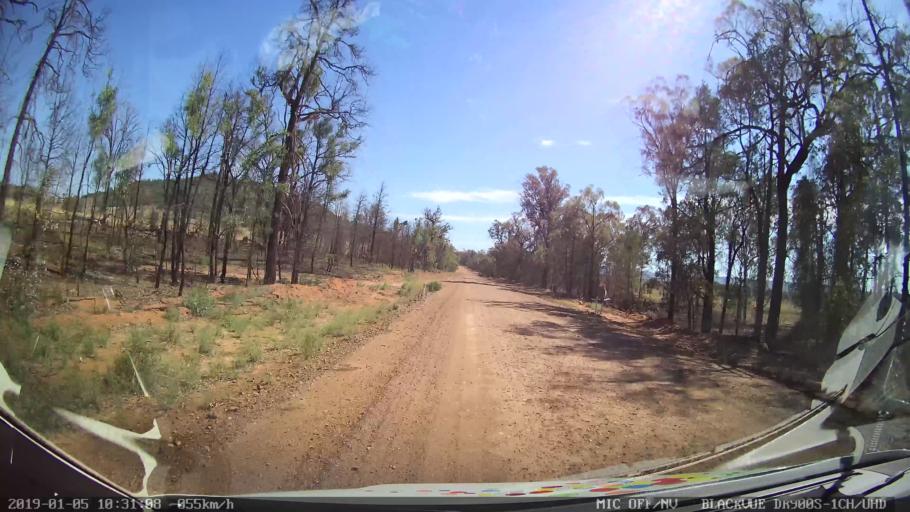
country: AU
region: New South Wales
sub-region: Gilgandra
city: Gilgandra
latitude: -31.5267
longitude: 148.9269
